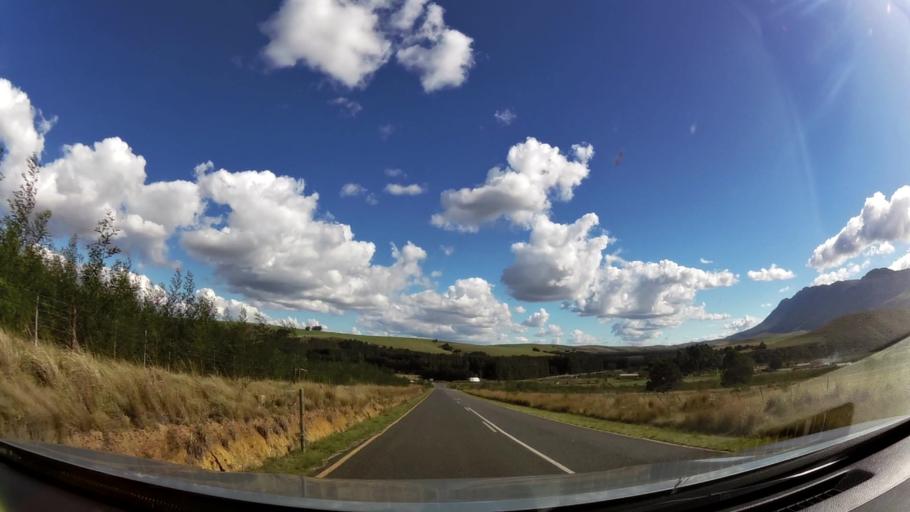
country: ZA
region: Western Cape
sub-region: Overberg District Municipality
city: Swellendam
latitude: -34.0253
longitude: 20.4238
